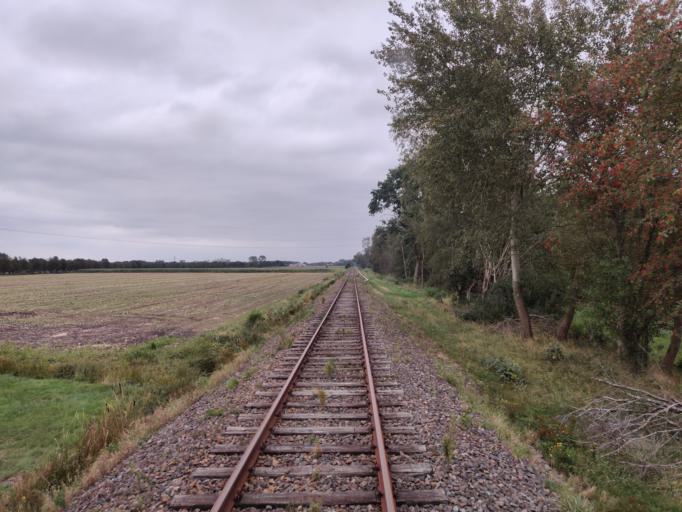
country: DE
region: Lower Saxony
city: Bei der Hohne
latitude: 53.4832
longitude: 9.0986
